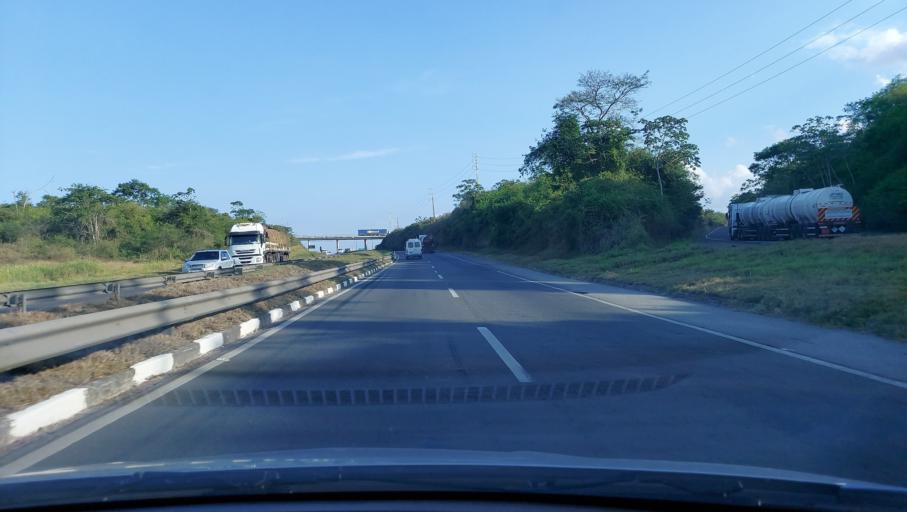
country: BR
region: Bahia
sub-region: Conceicao Do Jacuipe
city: Conceicao do Jacuipe
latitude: -12.3578
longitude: -38.8279
